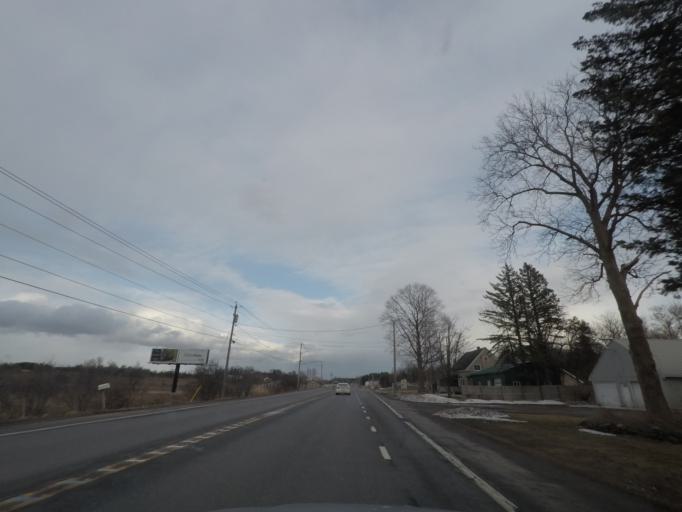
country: US
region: New York
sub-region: Oneida County
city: Vernon
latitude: 43.0750
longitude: -75.4592
